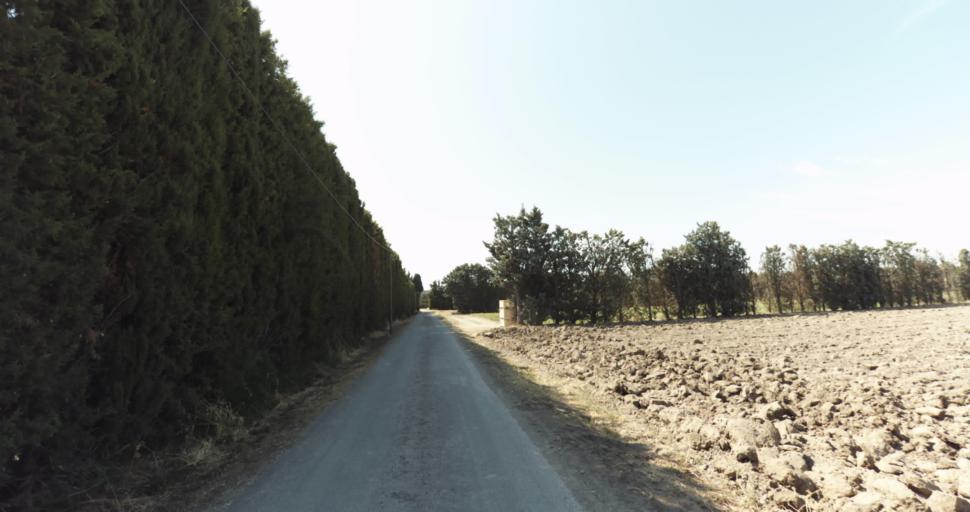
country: FR
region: Provence-Alpes-Cote d'Azur
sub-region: Departement du Vaucluse
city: Monteux
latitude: 44.0085
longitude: 4.9964
